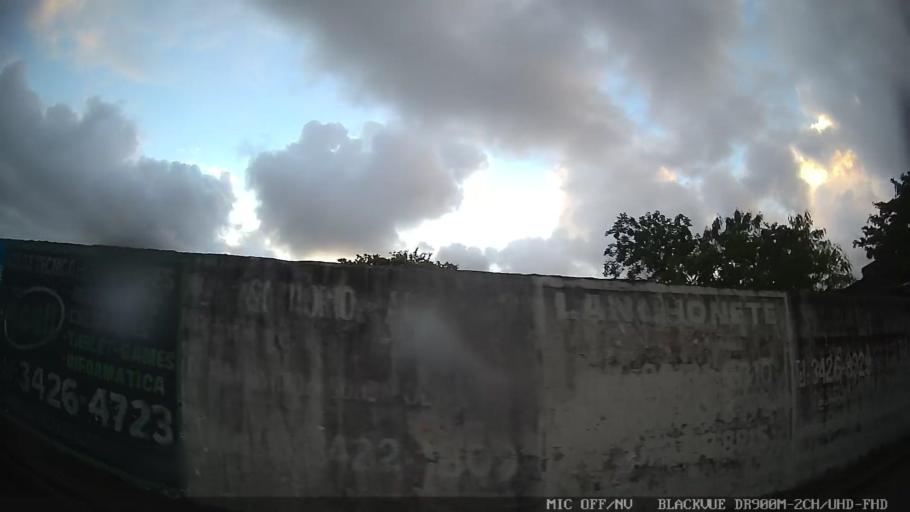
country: BR
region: Sao Paulo
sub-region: Itanhaem
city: Itanhaem
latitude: -24.1739
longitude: -46.7868
